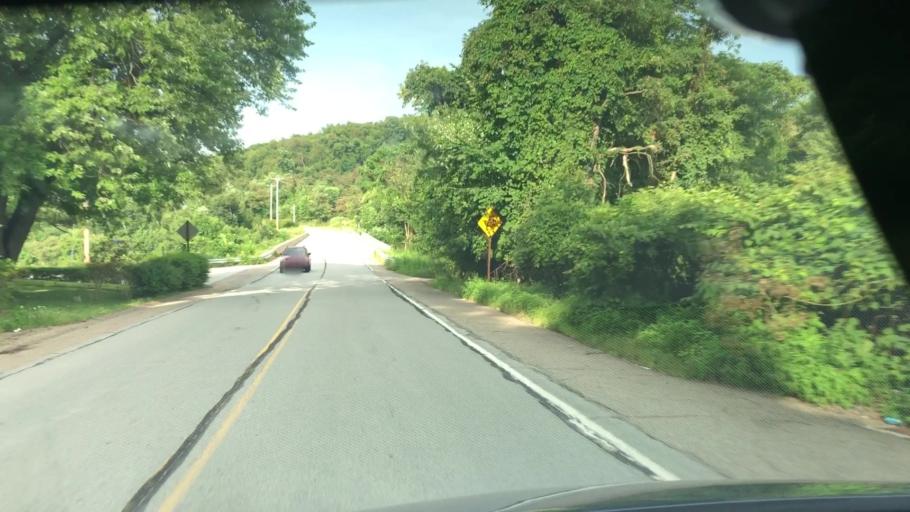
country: US
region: Pennsylvania
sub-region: Allegheny County
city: Aspinwall
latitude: 40.4740
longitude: -79.8834
